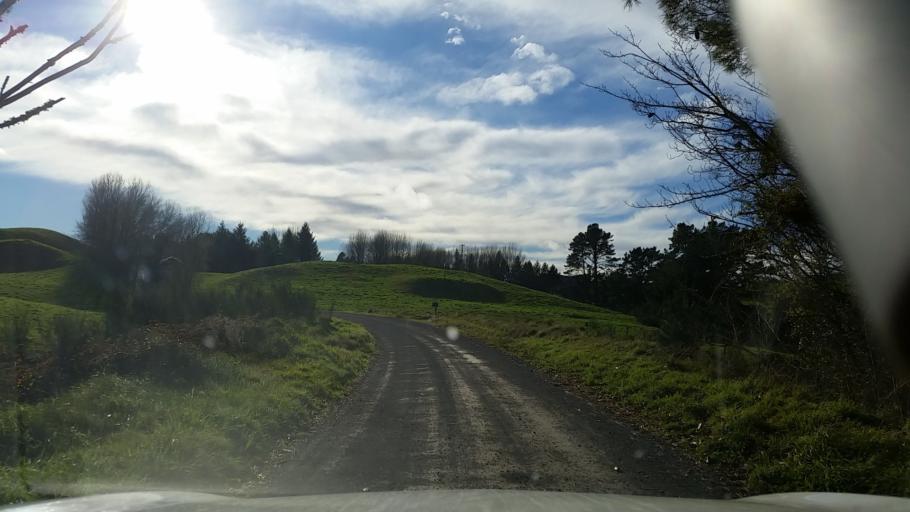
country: NZ
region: Waikato
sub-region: South Waikato District
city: Tokoroa
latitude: -38.3841
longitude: 176.0805
